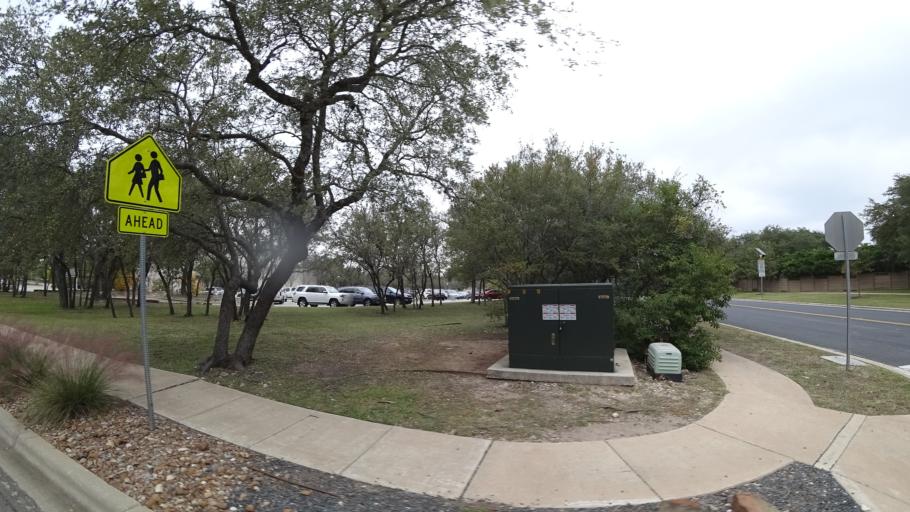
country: US
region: Texas
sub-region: Williamson County
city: Anderson Mill
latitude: 30.4361
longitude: -97.8240
